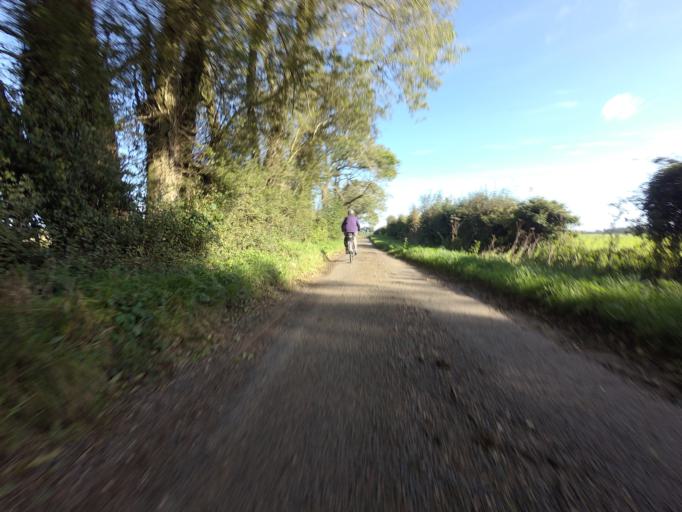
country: GB
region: England
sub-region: Norfolk
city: Fakenham
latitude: 52.8377
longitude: 0.6775
